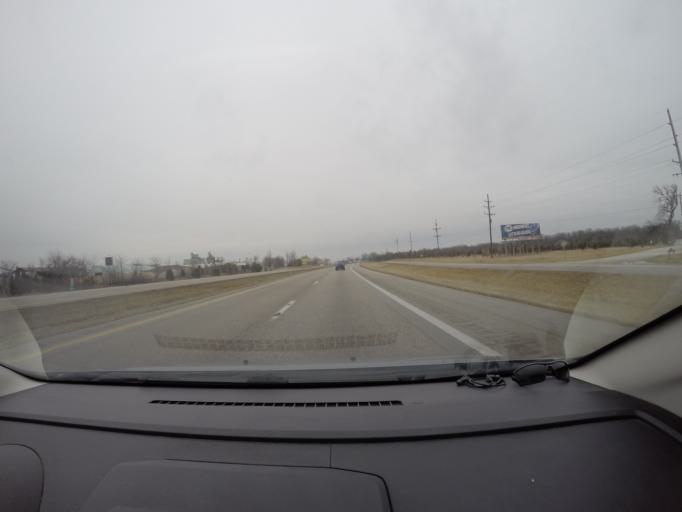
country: US
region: Missouri
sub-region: Montgomery County
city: Montgomery City
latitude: 38.8803
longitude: -91.3911
